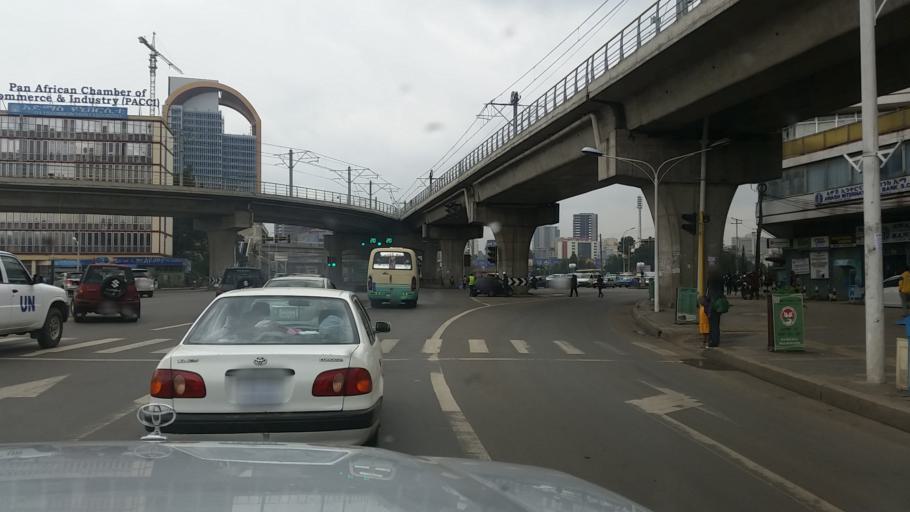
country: ET
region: Adis Abeba
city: Addis Ababa
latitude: 9.0114
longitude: 38.7601
